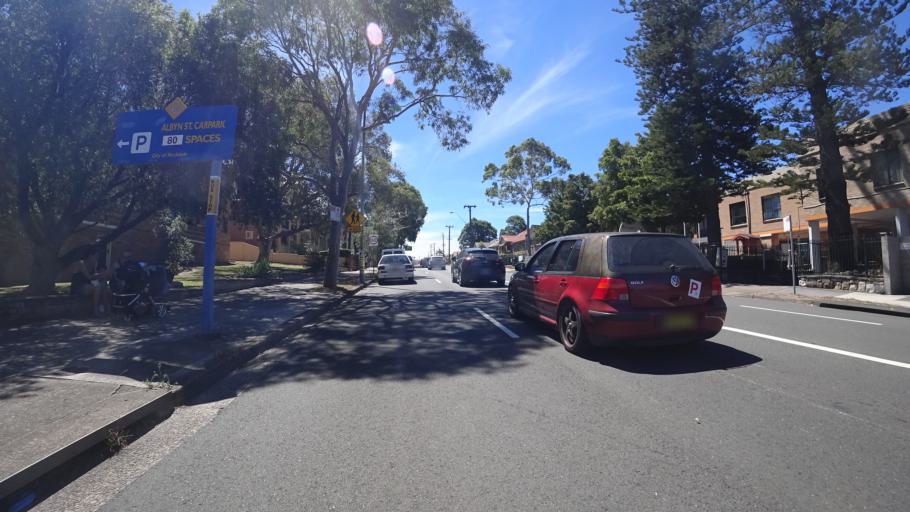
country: AU
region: New South Wales
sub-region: Rockdale
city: Bexley
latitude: -33.9501
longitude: 151.1295
